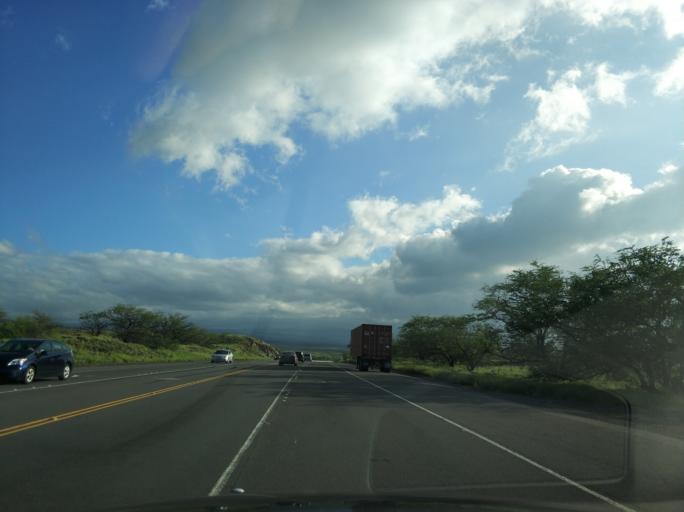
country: US
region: Hawaii
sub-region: Hawaii County
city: Waikoloa Village
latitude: 19.9737
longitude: -155.8206
